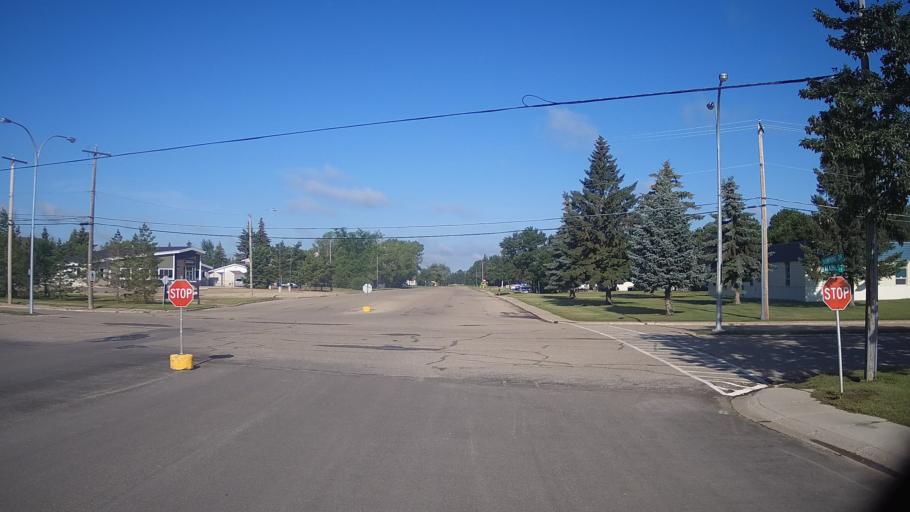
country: CA
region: Saskatchewan
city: Lanigan
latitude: 51.8507
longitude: -105.0307
